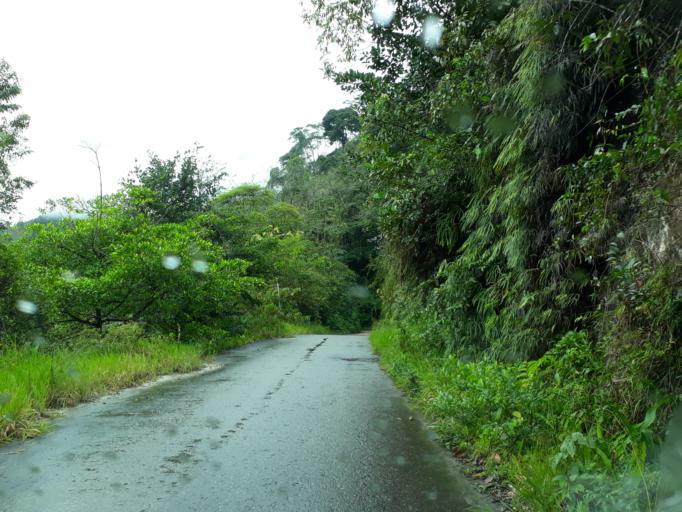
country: CO
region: Cundinamarca
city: Medina
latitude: 4.6753
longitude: -73.3236
